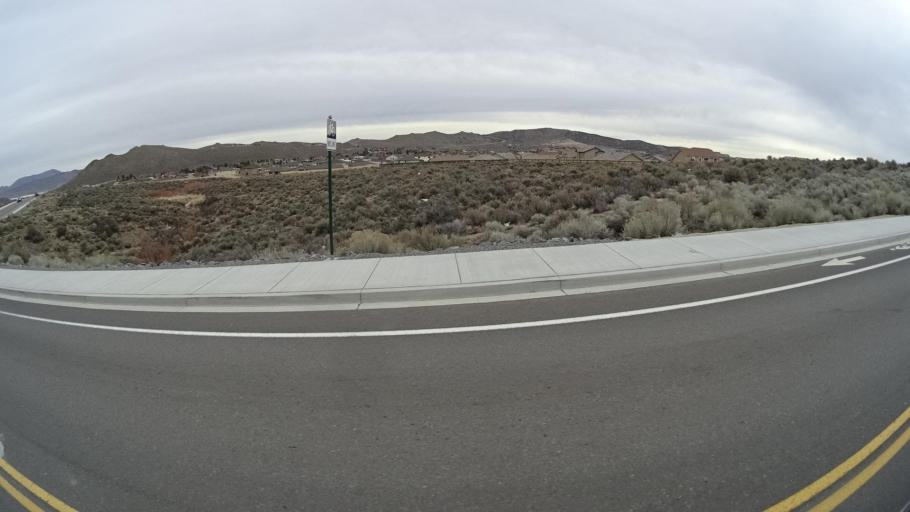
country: US
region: Nevada
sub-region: Washoe County
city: Golden Valley
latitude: 39.6083
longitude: -119.8447
